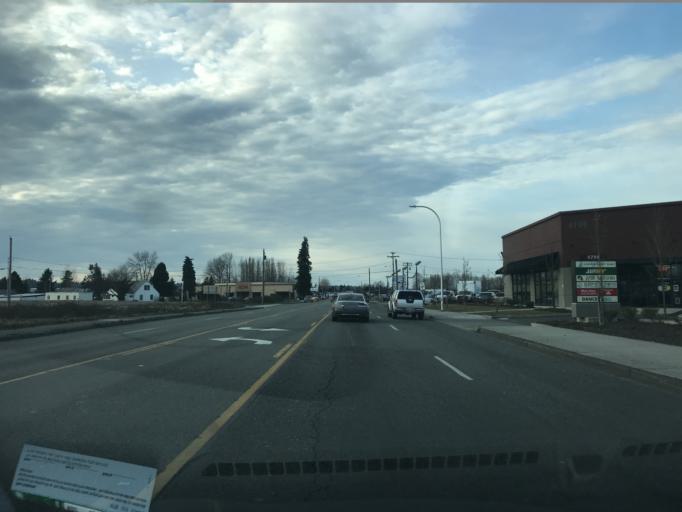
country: US
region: Washington
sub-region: King County
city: Kent
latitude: 47.3500
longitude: -122.2257
